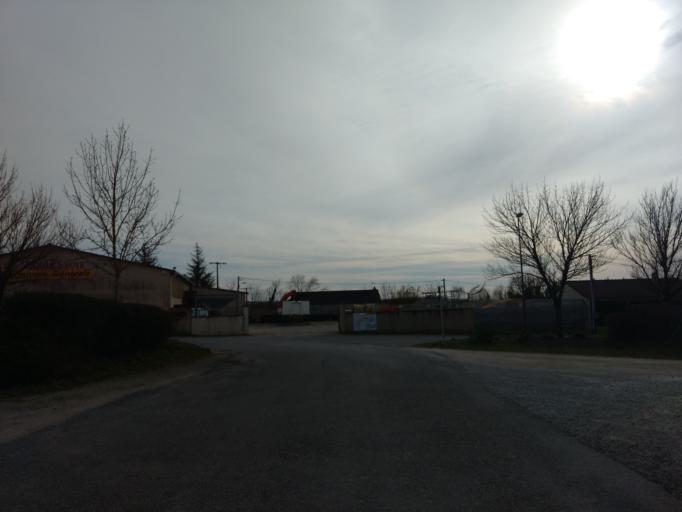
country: FR
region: Midi-Pyrenees
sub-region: Departement de l'Aveyron
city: Villeneuve
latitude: 44.3984
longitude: 2.0754
